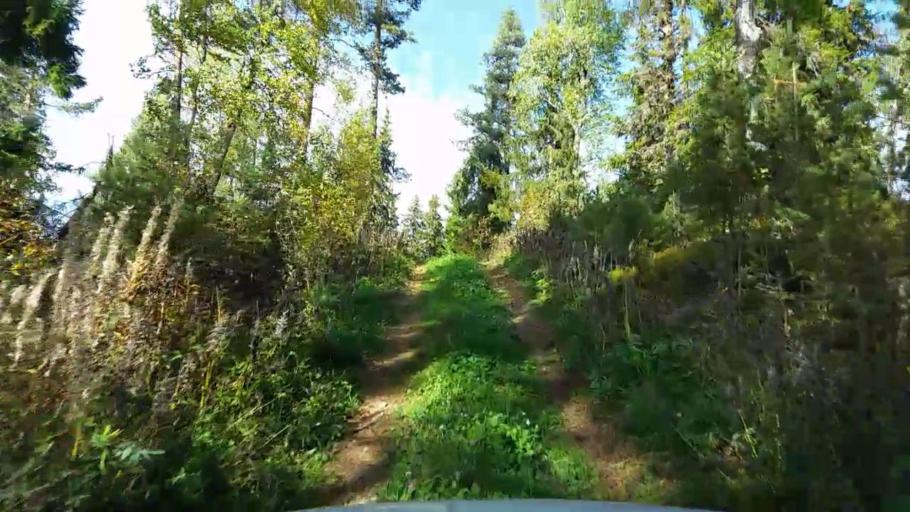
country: SE
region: Gaevleborg
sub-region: Ljusdals Kommun
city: Jaervsoe
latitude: 61.7831
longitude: 16.1869
